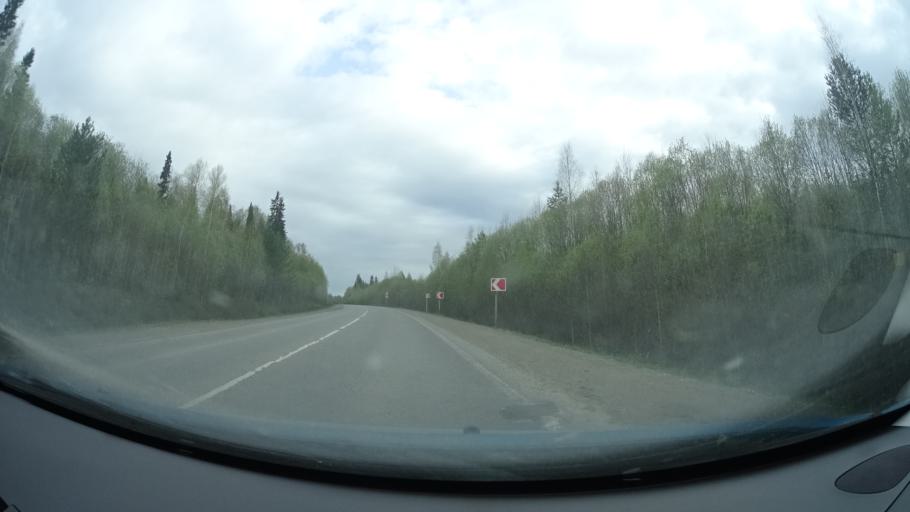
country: RU
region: Perm
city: Yugo-Kamskiy
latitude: 57.7485
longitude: 55.7116
